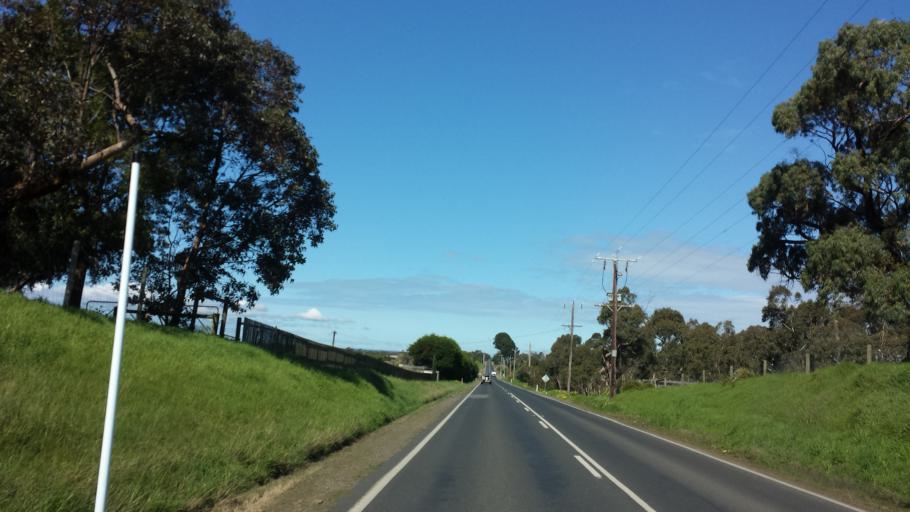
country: AU
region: Victoria
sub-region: Casey
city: Junction Village
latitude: -38.1428
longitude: 145.3223
